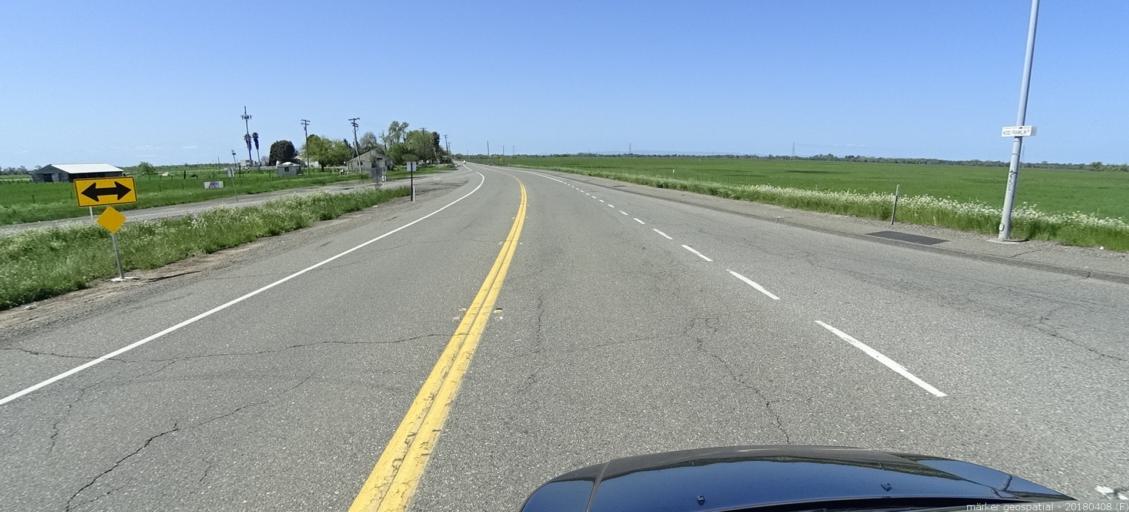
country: US
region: California
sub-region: Sacramento County
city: Laguna
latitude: 38.3753
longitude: -121.4794
